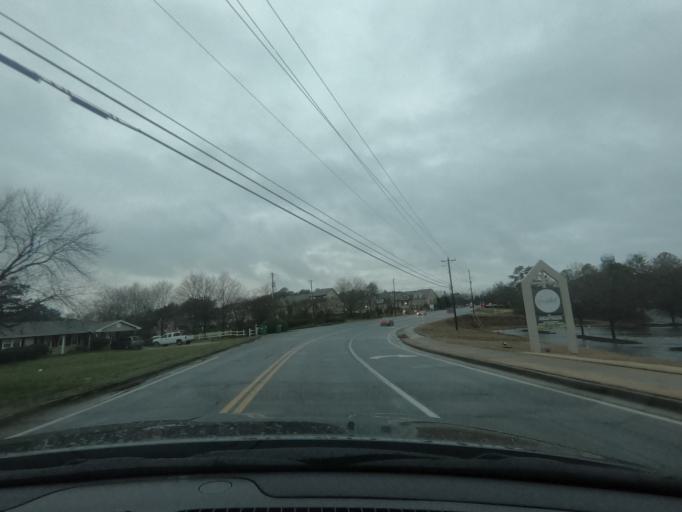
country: US
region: Georgia
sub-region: Cherokee County
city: Woodstock
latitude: 34.0913
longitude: -84.4925
